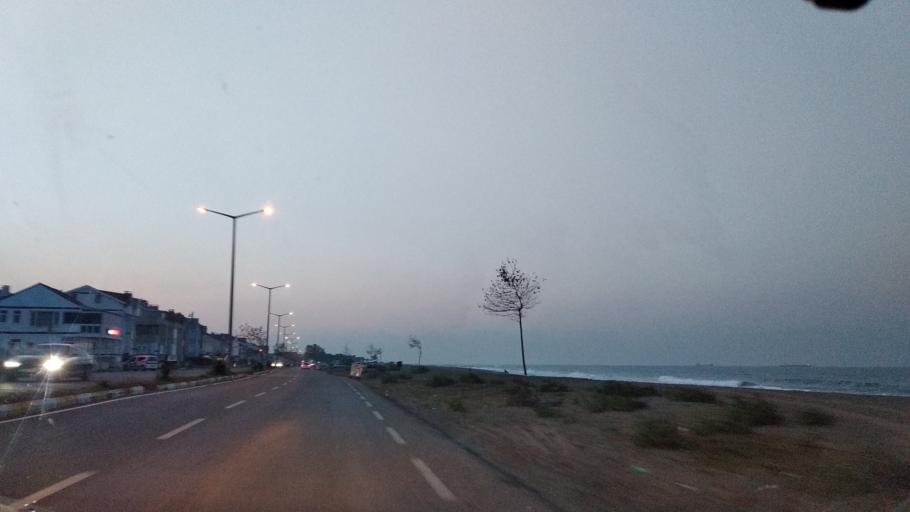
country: TR
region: Sakarya
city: Karasu
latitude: 41.0917
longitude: 30.7408
